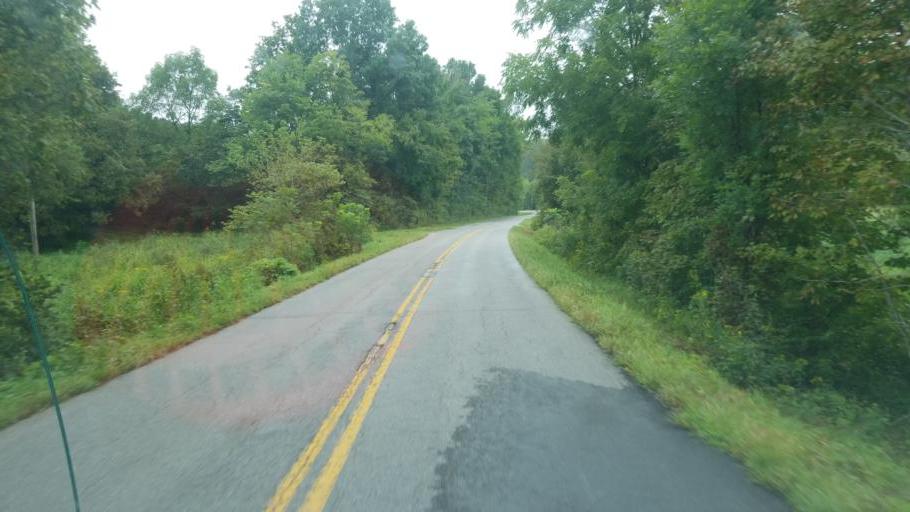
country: US
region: Kentucky
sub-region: Fleming County
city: Flemingsburg
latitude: 38.3660
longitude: -83.5340
